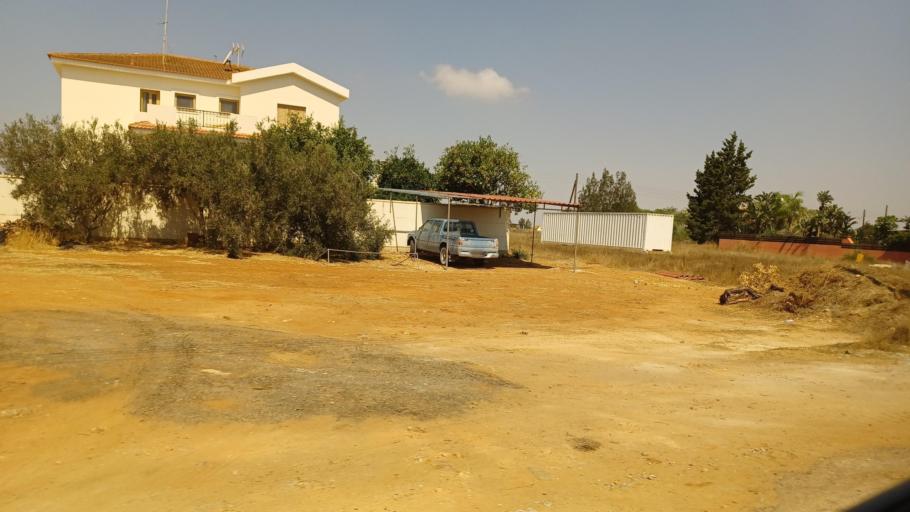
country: CY
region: Ammochostos
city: Frenaros
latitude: 35.0475
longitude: 33.9227
